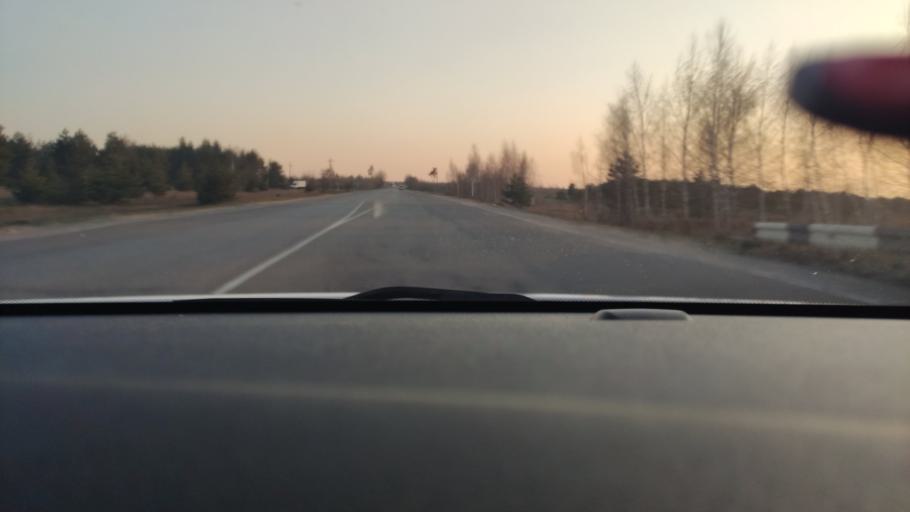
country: RU
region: Voronezj
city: Kolodeznyy
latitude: 51.3787
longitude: 39.2152
